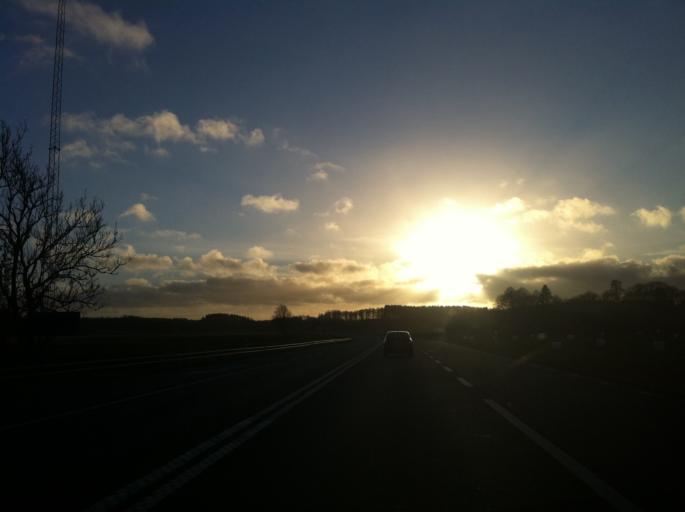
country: SE
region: Skane
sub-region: Hassleholms Kommun
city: Tormestorp
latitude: 56.0699
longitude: 13.7409
